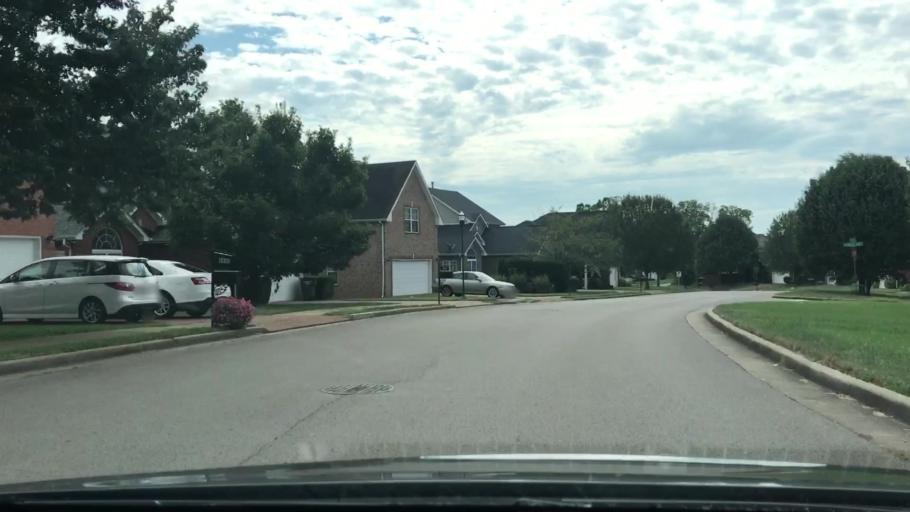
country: US
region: Tennessee
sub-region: Williamson County
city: Nolensville
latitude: 36.0057
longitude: -86.6936
